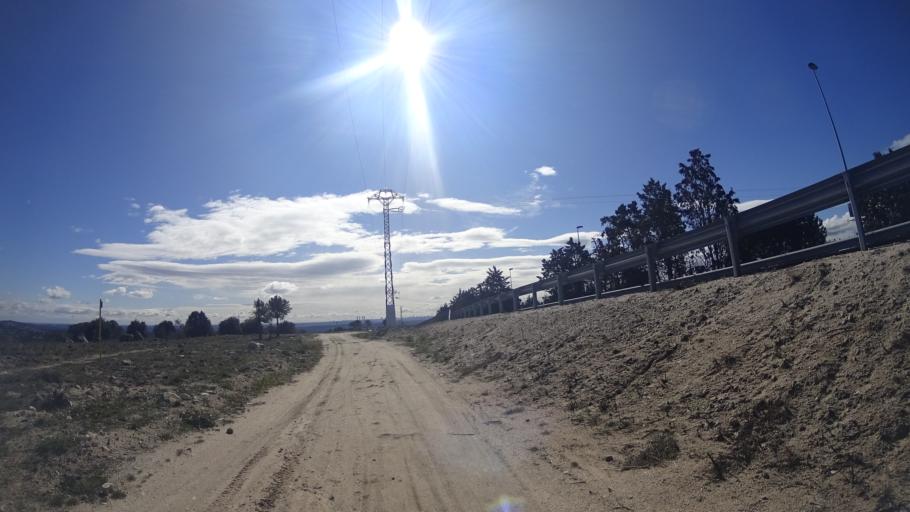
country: ES
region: Madrid
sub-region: Provincia de Madrid
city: Torrelodones
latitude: 40.5685
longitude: -3.9154
